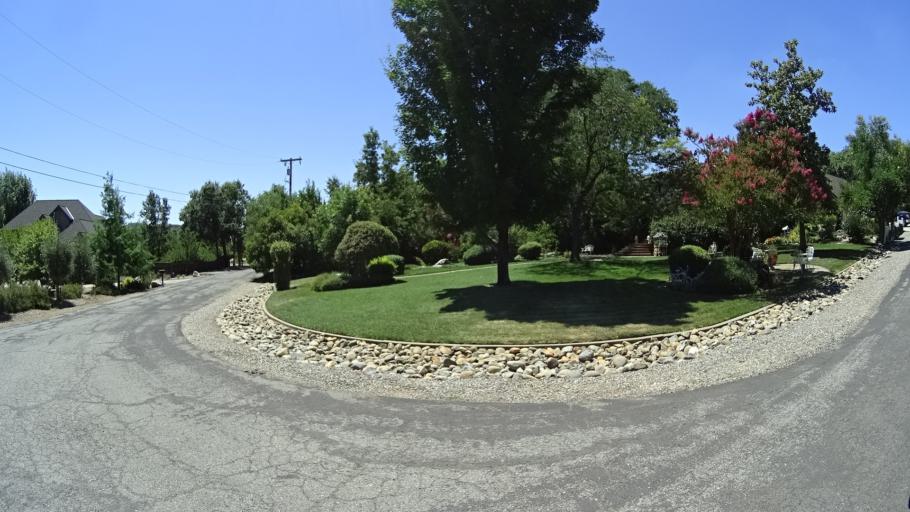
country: US
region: California
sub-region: Calaveras County
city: Murphys
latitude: 38.1325
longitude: -120.4403
